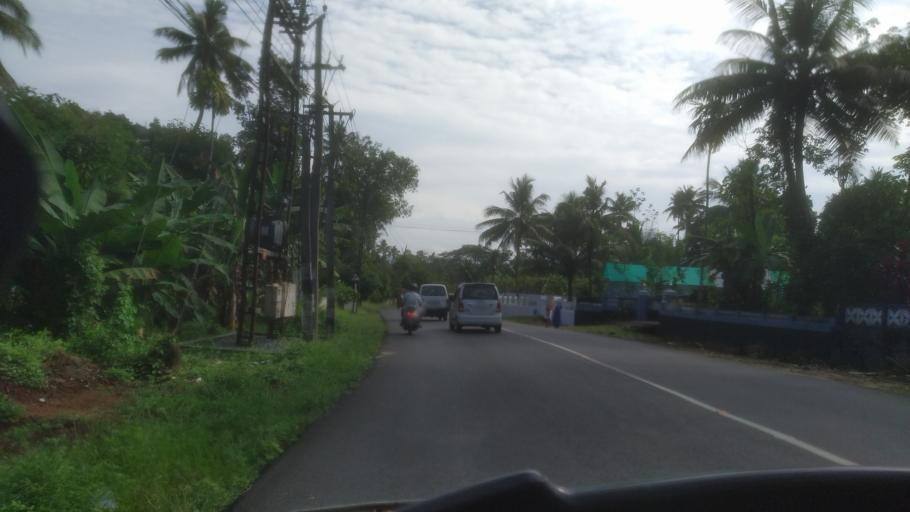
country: IN
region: Kerala
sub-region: Ernakulam
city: Kotamangalam
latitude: 10.0584
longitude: 76.6765
